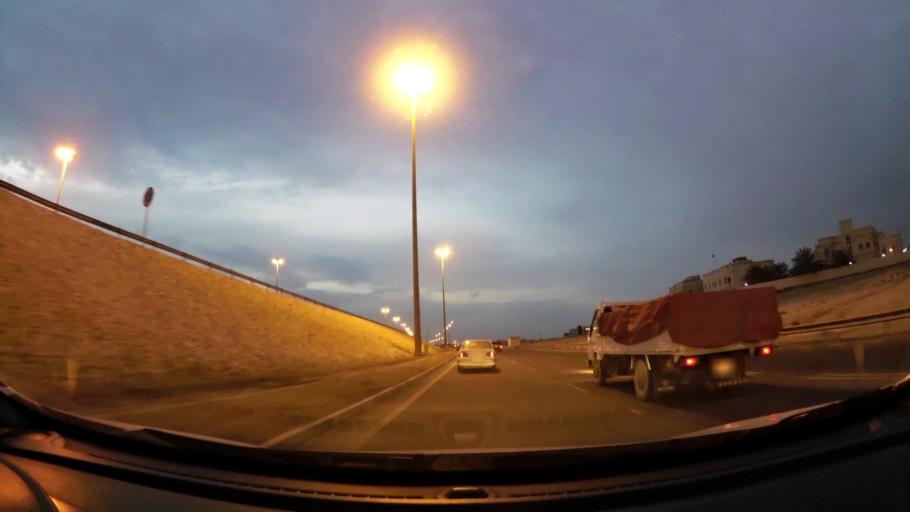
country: BH
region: Central Governorate
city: Madinat Hamad
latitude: 26.1407
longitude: 50.5109
